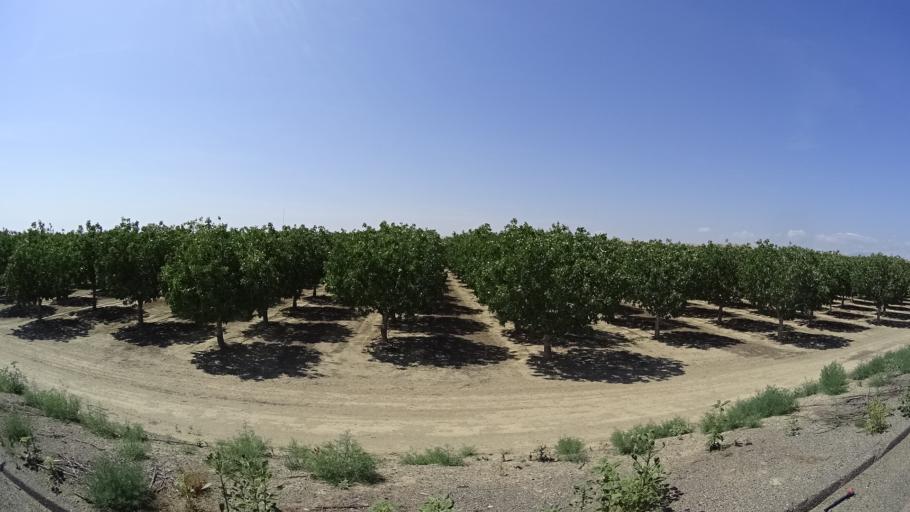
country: US
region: California
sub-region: Kings County
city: Kettleman City
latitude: 36.0724
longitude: -120.0190
